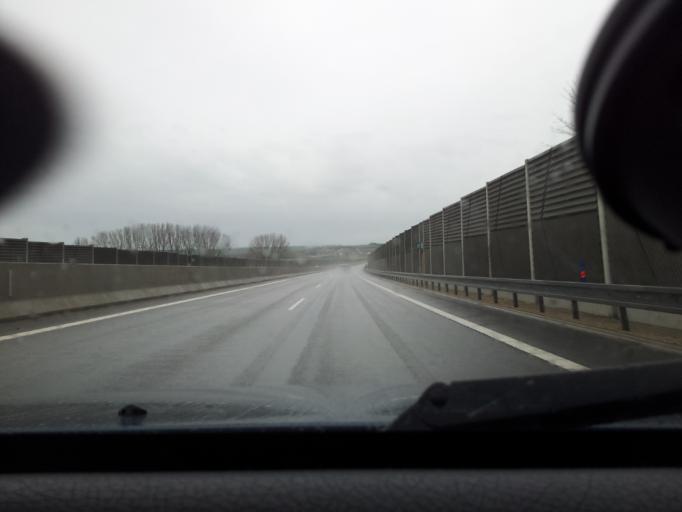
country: SK
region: Nitriansky
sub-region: Okres Nitra
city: Nitra
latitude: 48.2985
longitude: 18.1228
